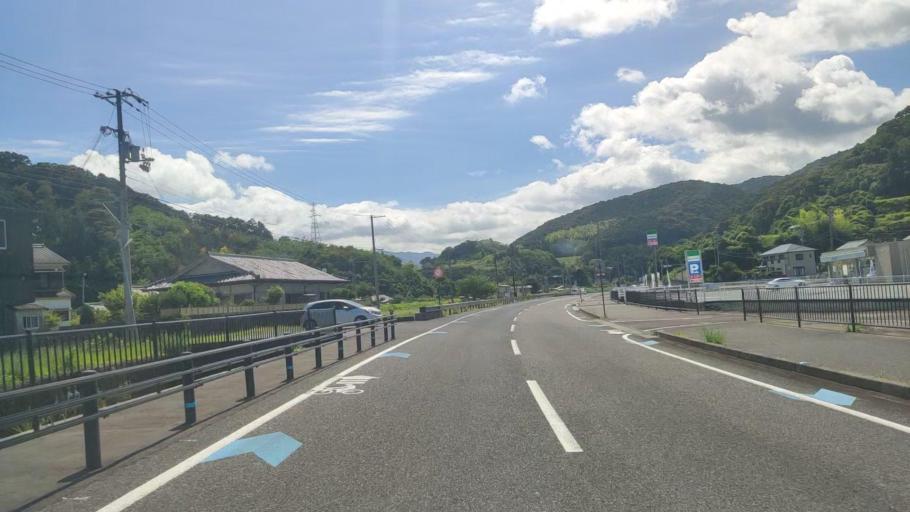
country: JP
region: Wakayama
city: Shingu
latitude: 33.7404
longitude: 136.0016
